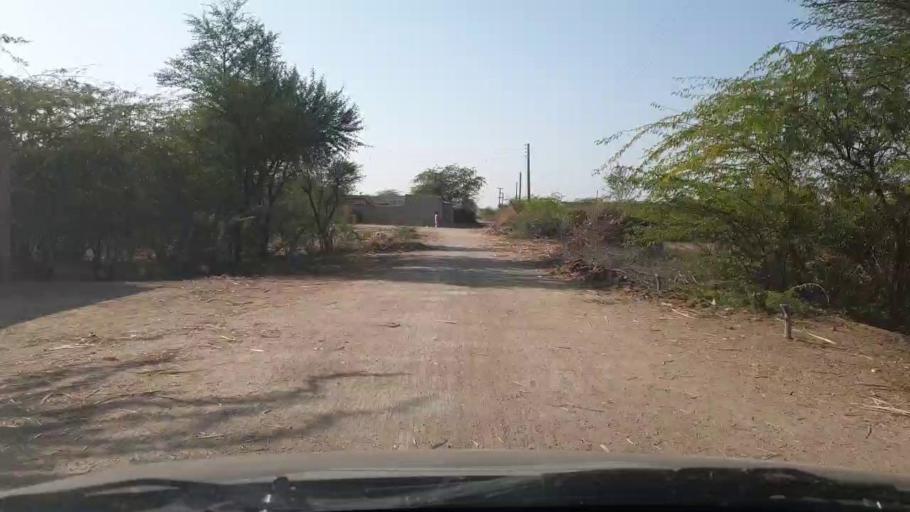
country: PK
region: Sindh
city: Samaro
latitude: 25.1676
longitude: 69.2812
